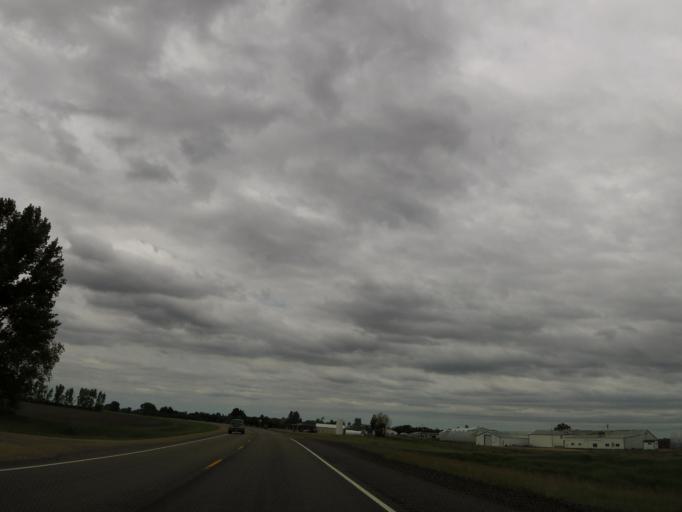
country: US
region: North Dakota
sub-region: Walsh County
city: Grafton
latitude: 48.6076
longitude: -97.4478
